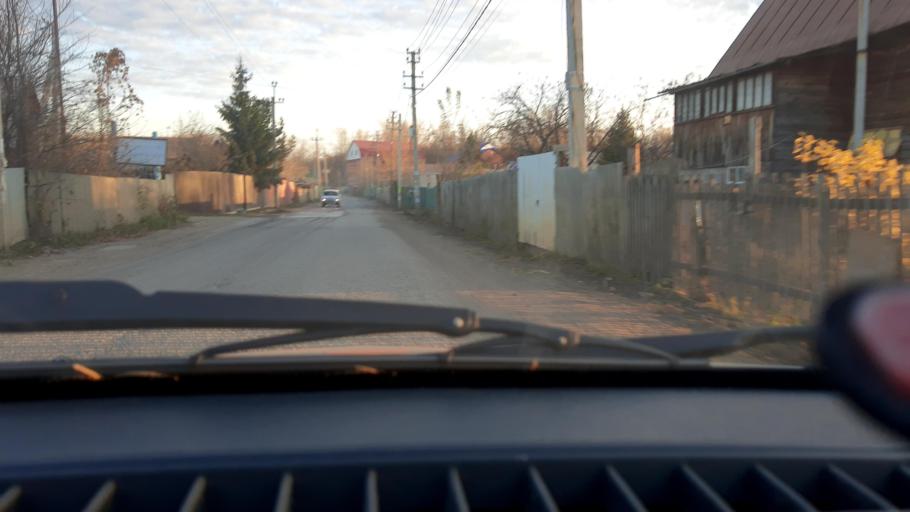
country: RU
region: Bashkortostan
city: Ufa
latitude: 54.6938
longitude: 55.9012
